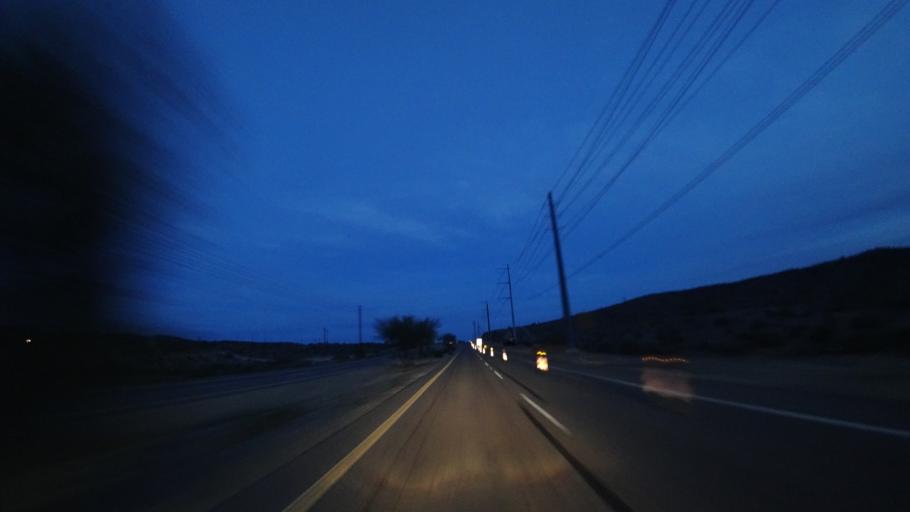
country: US
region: Arizona
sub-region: Maricopa County
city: Laveen
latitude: 33.2910
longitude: -112.0713
